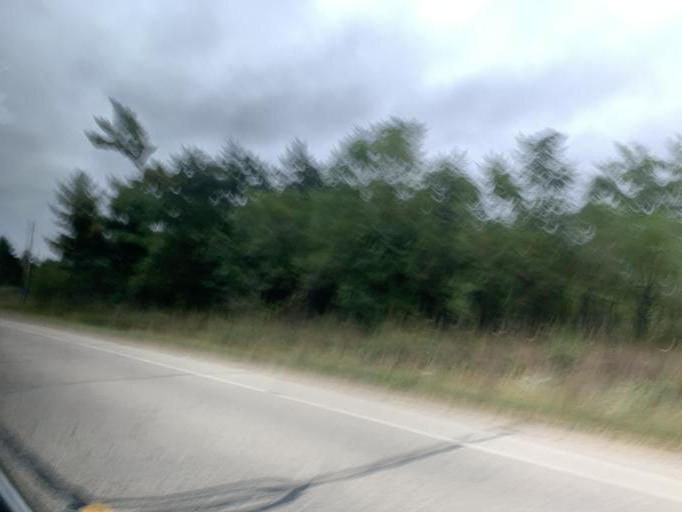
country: US
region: Wisconsin
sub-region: Grant County
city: Boscobel
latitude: 43.2054
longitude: -90.6081
